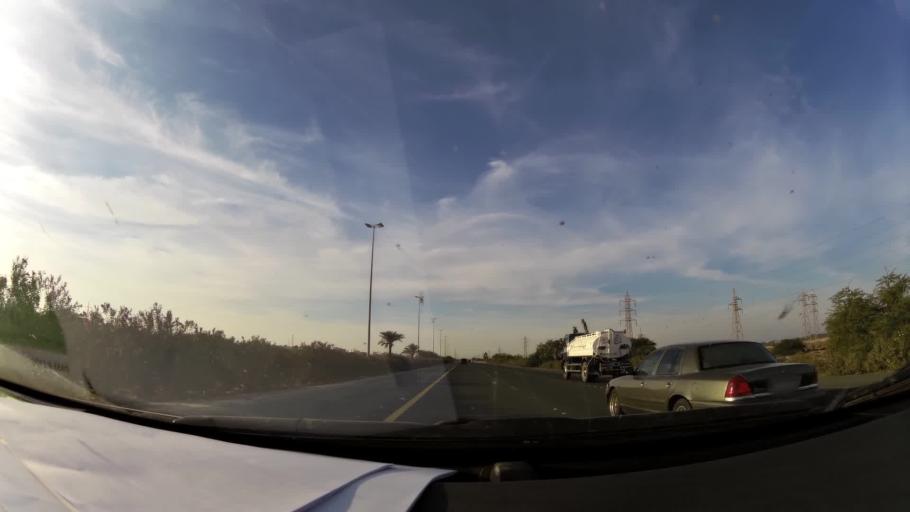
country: KW
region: Al Ahmadi
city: Al Fahahil
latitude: 28.9493
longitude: 48.1771
